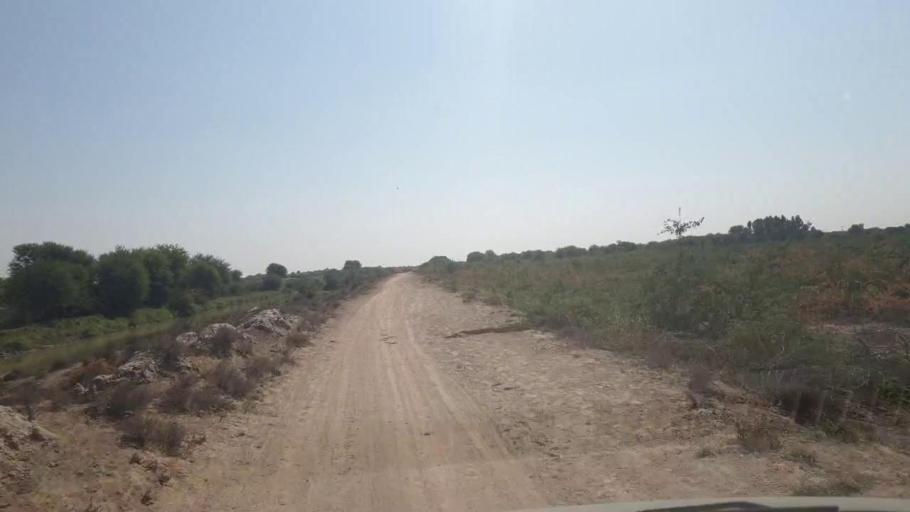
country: PK
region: Sindh
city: Digri
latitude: 24.9319
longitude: 69.1640
